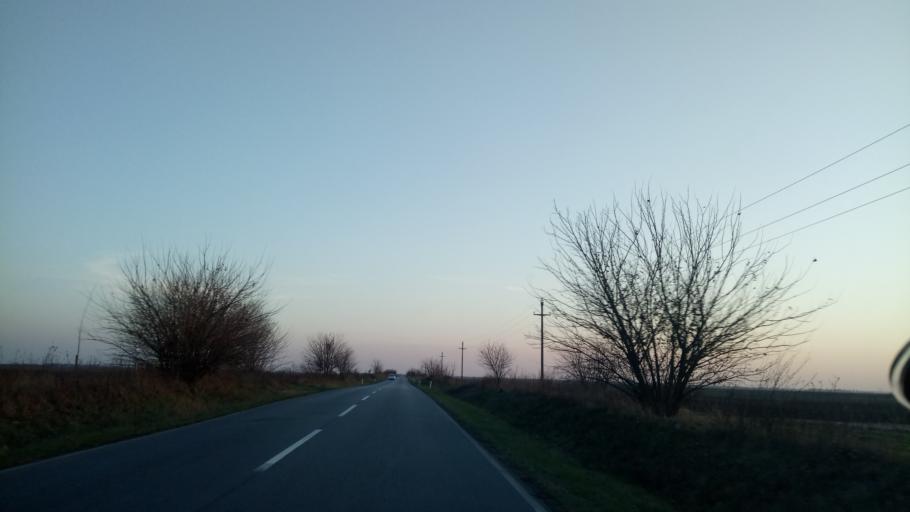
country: RS
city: Surduk
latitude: 45.0526
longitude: 20.3317
